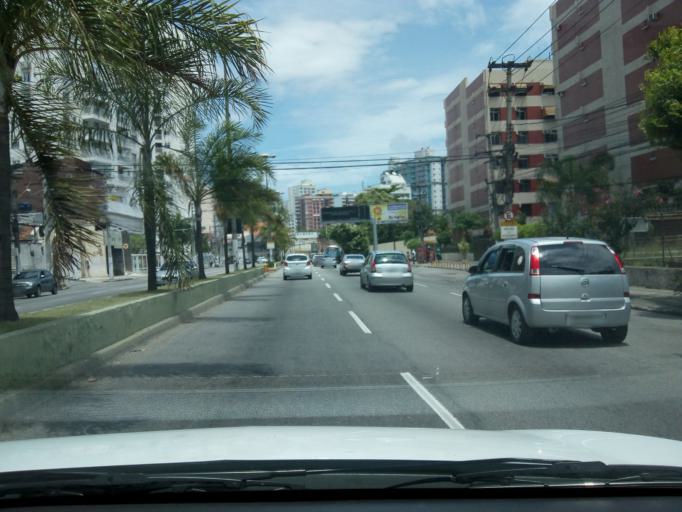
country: BR
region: Rio de Janeiro
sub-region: Niteroi
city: Niteroi
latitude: -22.8973
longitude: -43.1121
